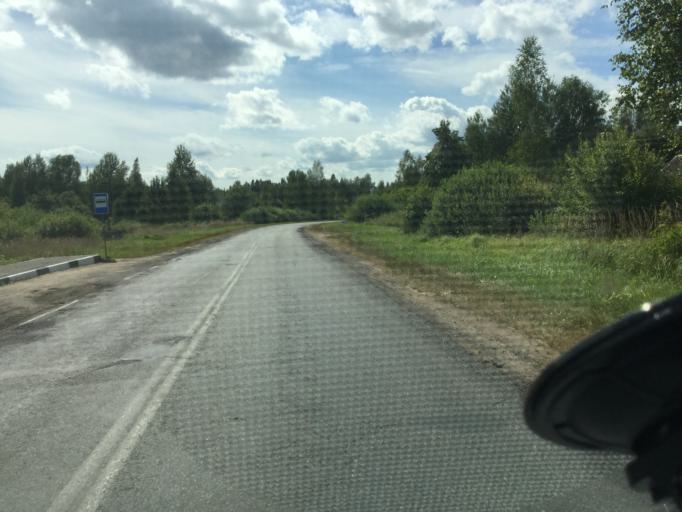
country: BY
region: Vitebsk
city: Chashniki
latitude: 55.2878
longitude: 29.3620
